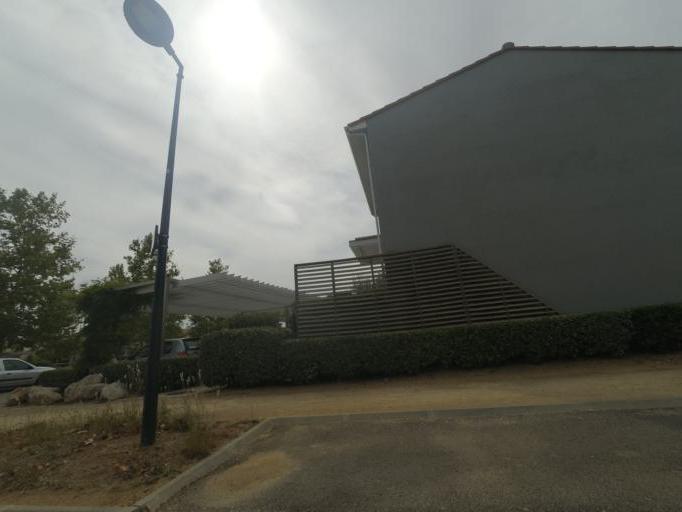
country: FR
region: Languedoc-Roussillon
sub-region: Departement du Gard
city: Aimargues
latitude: 43.7008
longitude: 4.2003
